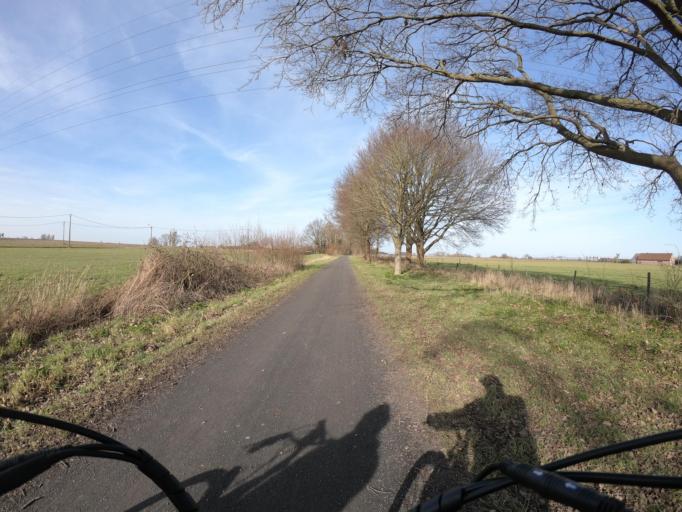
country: BE
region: Flanders
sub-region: Provincie West-Vlaanderen
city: Ledegem
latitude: 50.8323
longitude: 3.1237
